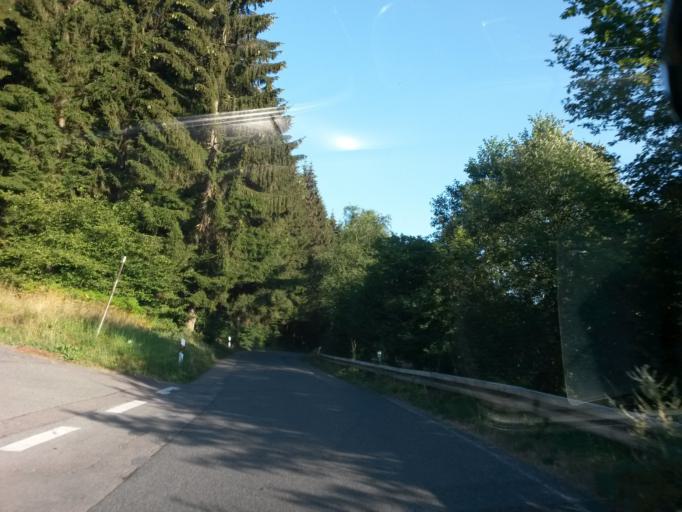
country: DE
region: North Rhine-Westphalia
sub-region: Regierungsbezirk Koln
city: Lindlar
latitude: 51.0708
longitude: 7.3536
